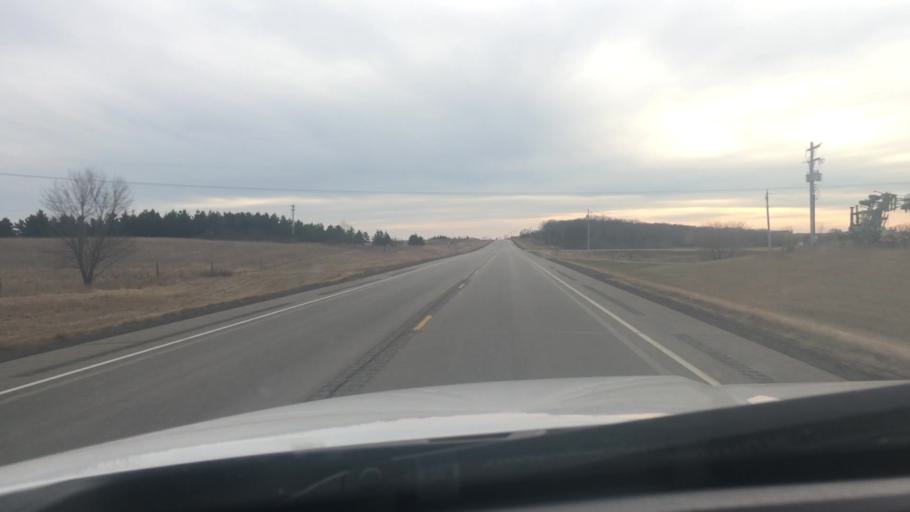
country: US
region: Minnesota
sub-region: Otter Tail County
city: Perham
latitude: 46.3202
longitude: -95.7185
